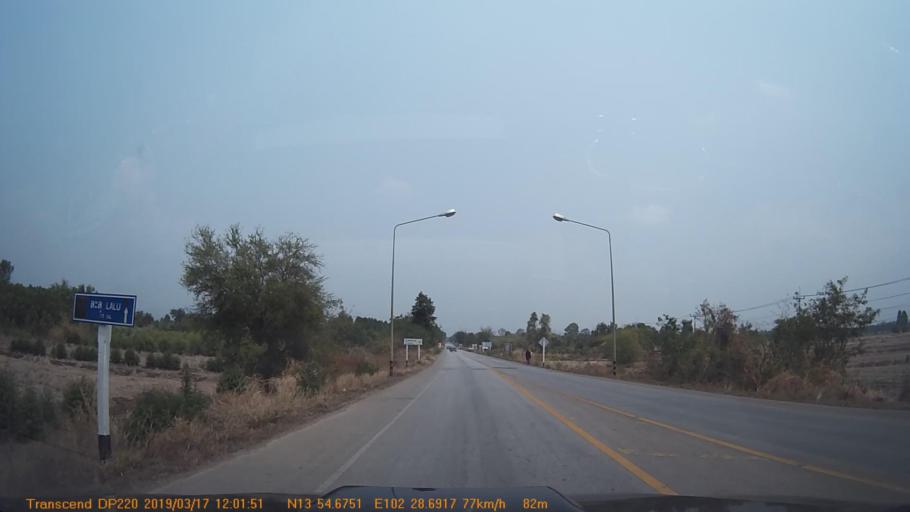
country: TH
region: Sa Kaeo
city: Khok Sung
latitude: 13.9115
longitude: 102.4783
